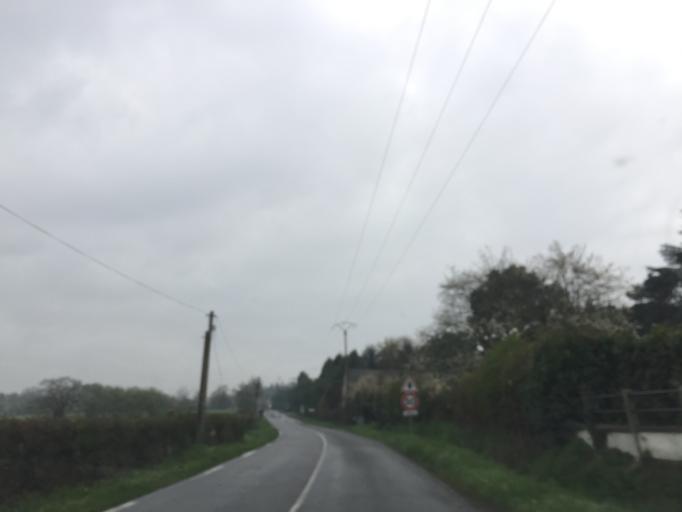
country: FR
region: Pays de la Loire
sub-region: Departement de la Loire-Atlantique
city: Suce-sur-Erdre
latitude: 47.3521
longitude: -1.5309
